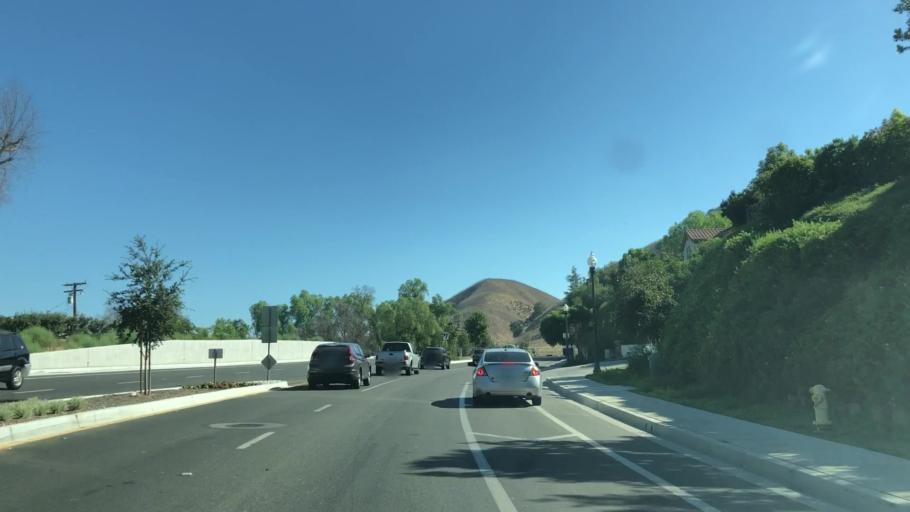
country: US
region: California
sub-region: Los Angeles County
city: Agoura
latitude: 34.1418
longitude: -118.6997
